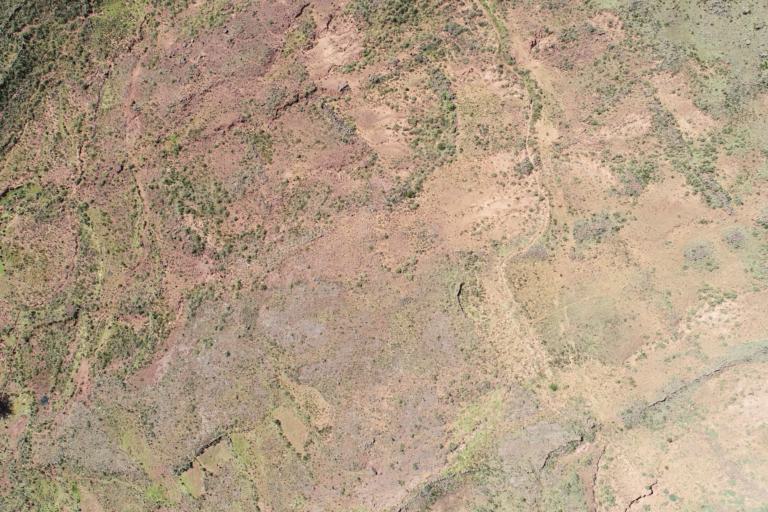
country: BO
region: La Paz
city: Tiahuanaco
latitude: -16.6059
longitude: -68.7780
